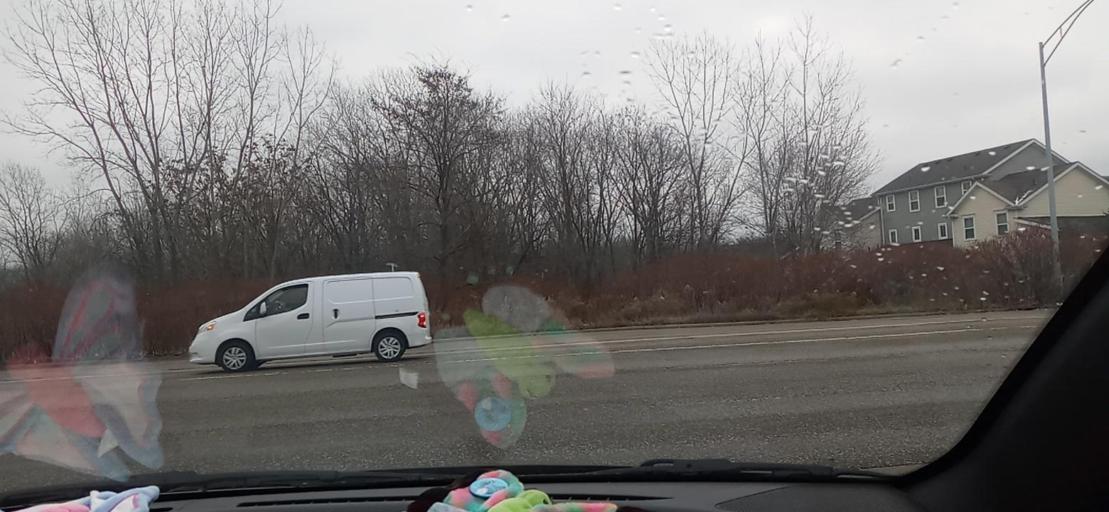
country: US
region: Ohio
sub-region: Summit County
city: Sawyerwood
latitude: 41.0261
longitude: -81.4627
